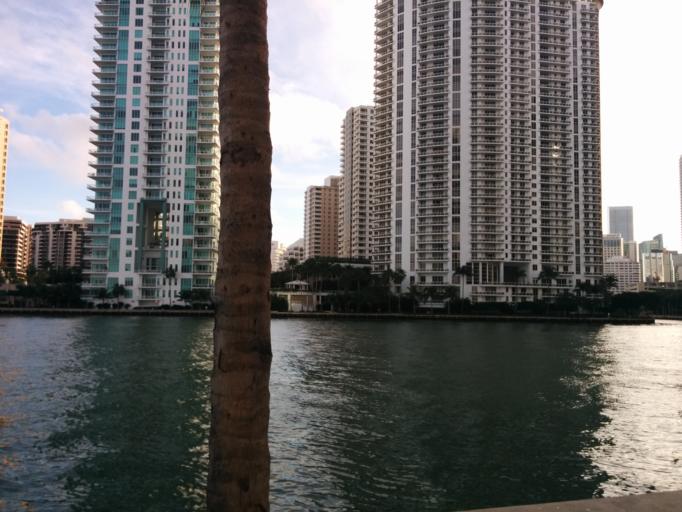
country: US
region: Florida
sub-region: Miami-Dade County
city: Miami
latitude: 25.7711
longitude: -80.1865
